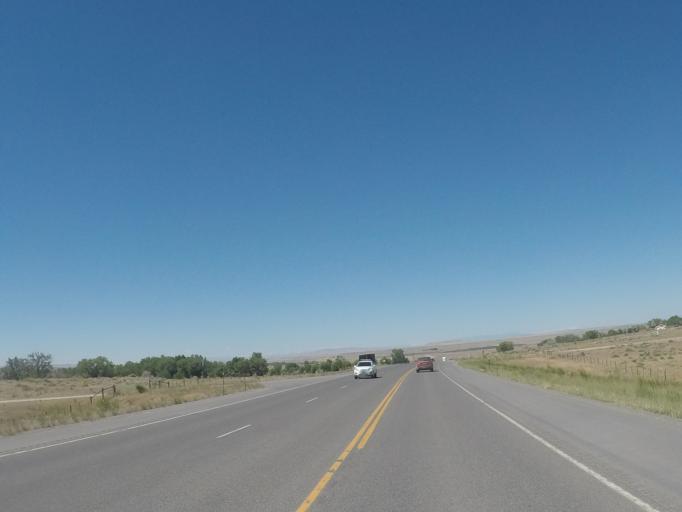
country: US
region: Wyoming
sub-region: Big Horn County
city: Greybull
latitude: 44.4923
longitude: -108.0213
